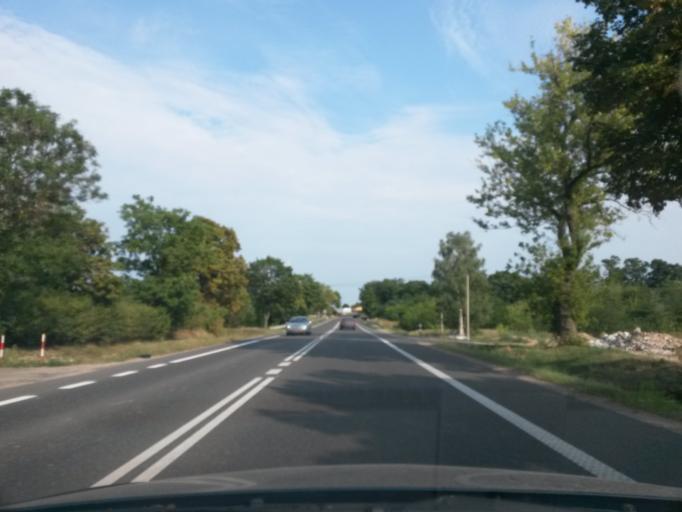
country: PL
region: Masovian Voivodeship
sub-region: Powiat sierpecki
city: Sierpc
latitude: 52.8510
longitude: 19.7009
